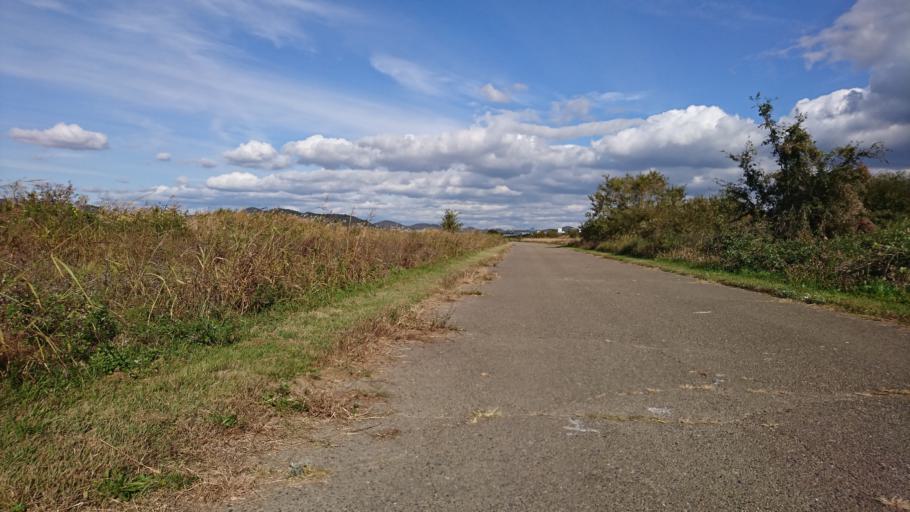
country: JP
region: Hyogo
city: Kakogawacho-honmachi
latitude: 34.7844
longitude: 134.8625
